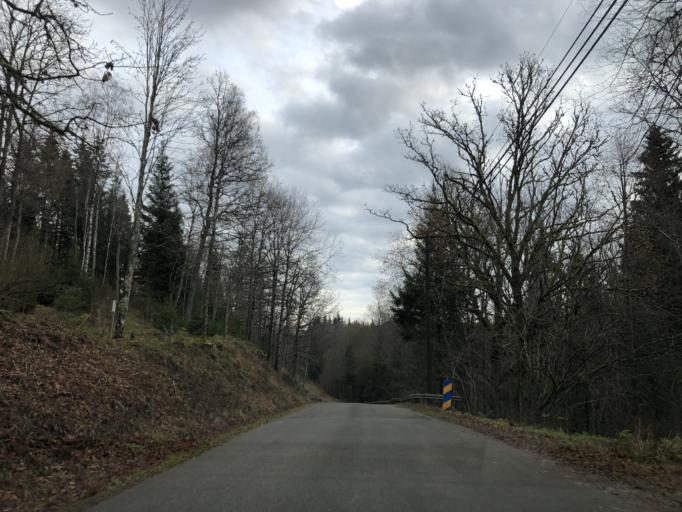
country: SE
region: Vaestra Goetaland
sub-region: Ulricehamns Kommun
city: Ulricehamn
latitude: 57.7276
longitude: 13.3378
